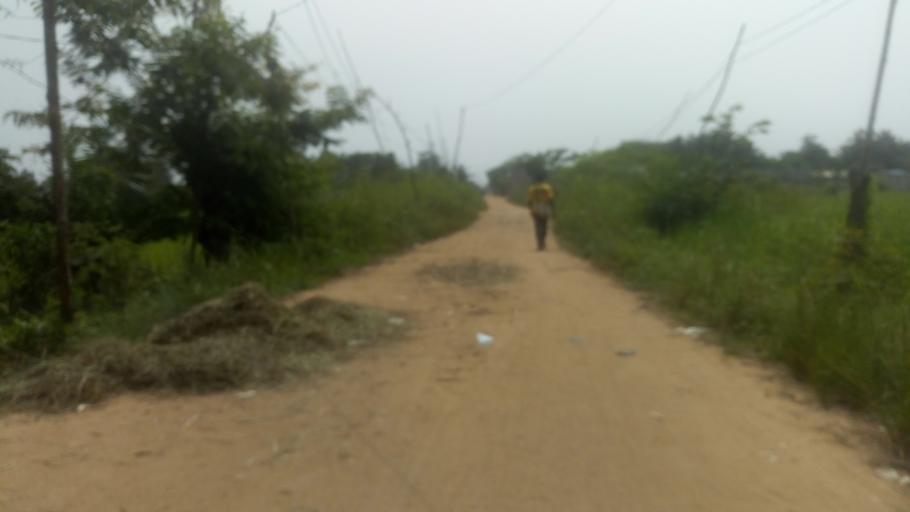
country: TG
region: Maritime
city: Lome
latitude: 6.2810
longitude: 1.2032
